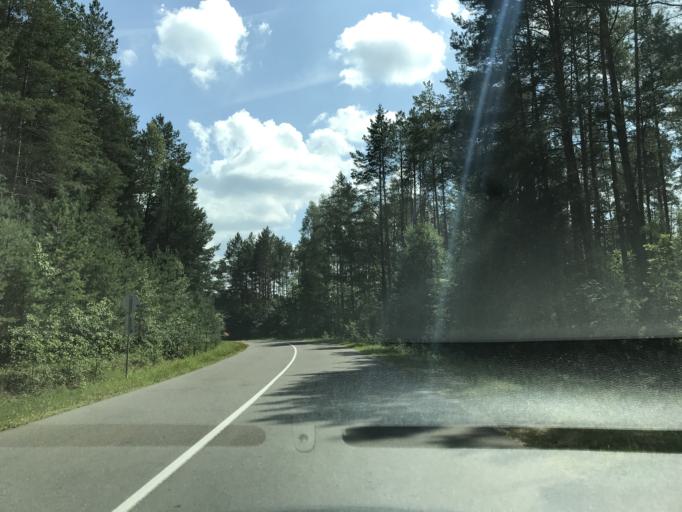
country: BY
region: Minsk
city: Rakaw
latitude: 53.9968
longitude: 26.9871
